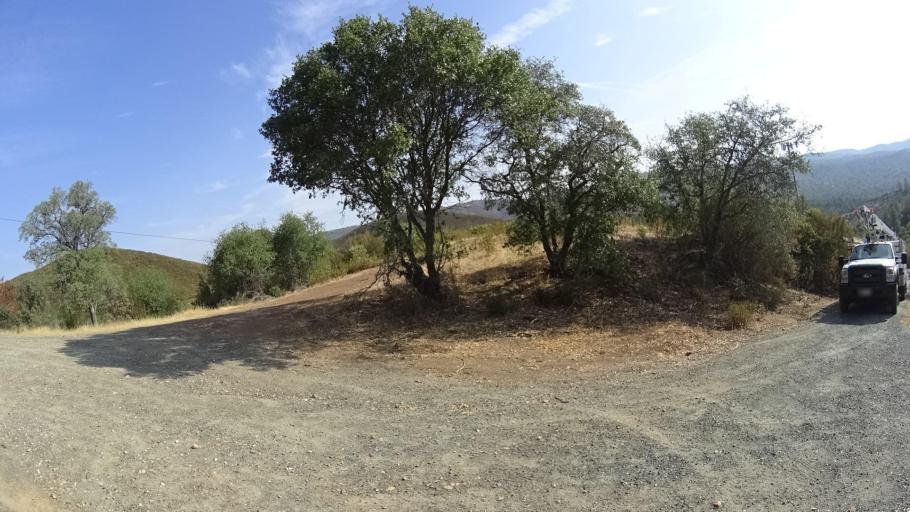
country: US
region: California
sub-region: Tuolumne County
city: Tuolumne City
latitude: 37.7329
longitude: -120.2351
